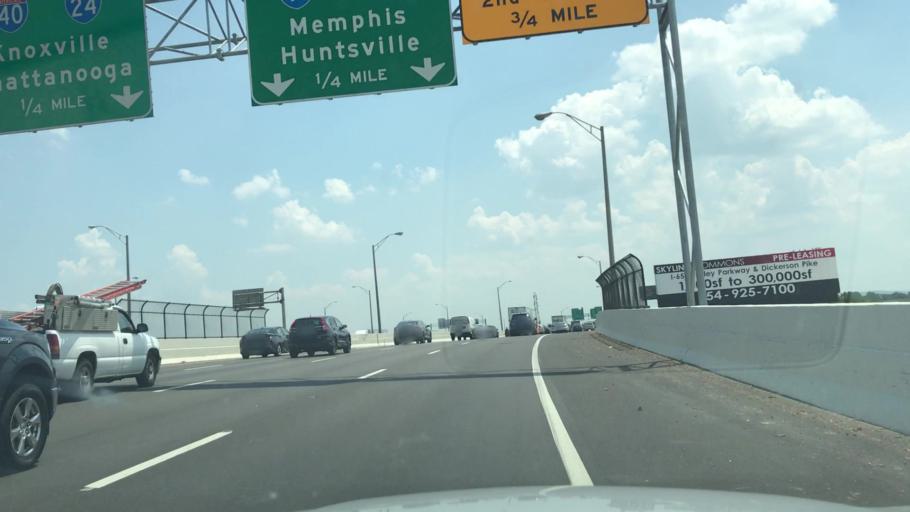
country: US
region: Tennessee
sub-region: Davidson County
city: Nashville
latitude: 36.1611
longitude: -86.7607
